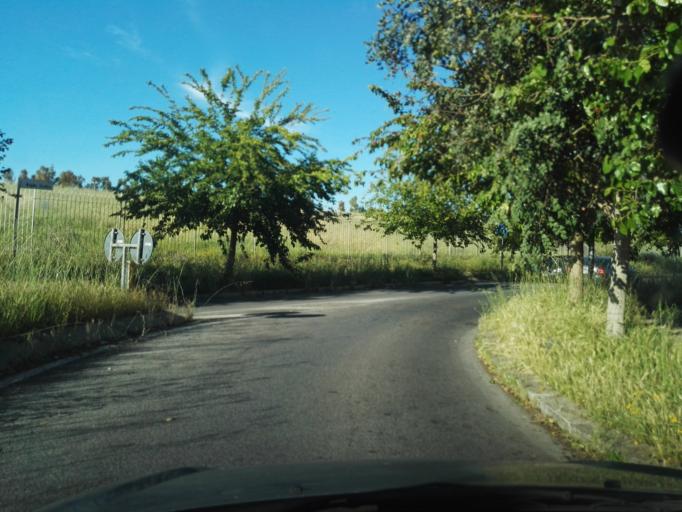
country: IT
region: Latium
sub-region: Citta metropolitana di Roma Capitale
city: Selcetta
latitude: 41.7688
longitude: 12.4710
